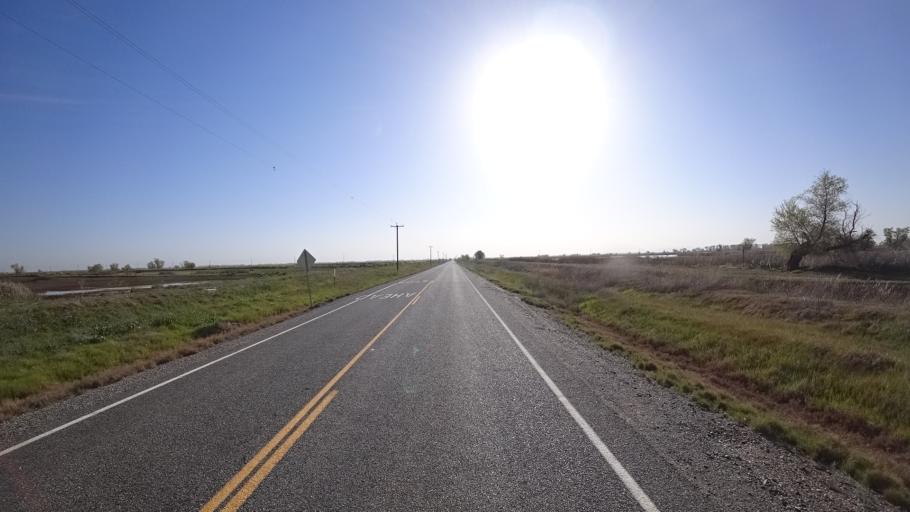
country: US
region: California
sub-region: Glenn County
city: Willows
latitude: 39.4071
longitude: -122.1897
